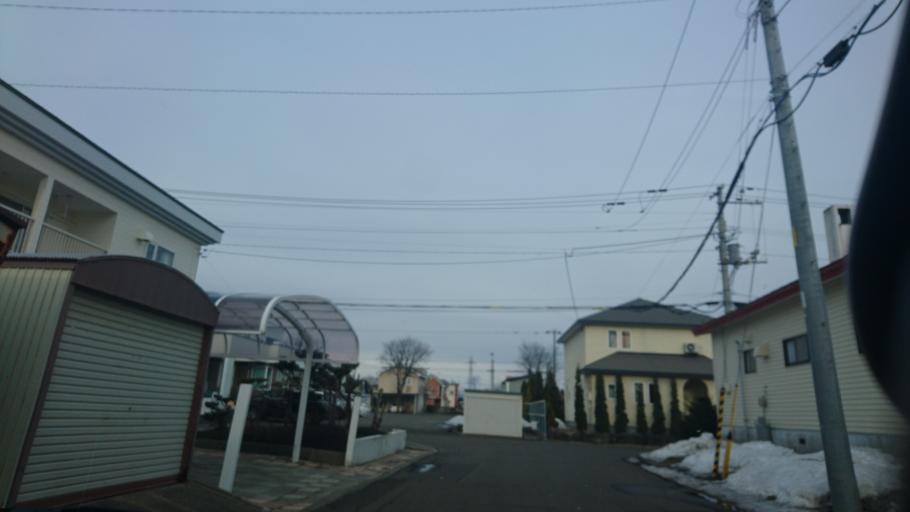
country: JP
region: Hokkaido
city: Otofuke
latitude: 42.9969
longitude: 143.1909
